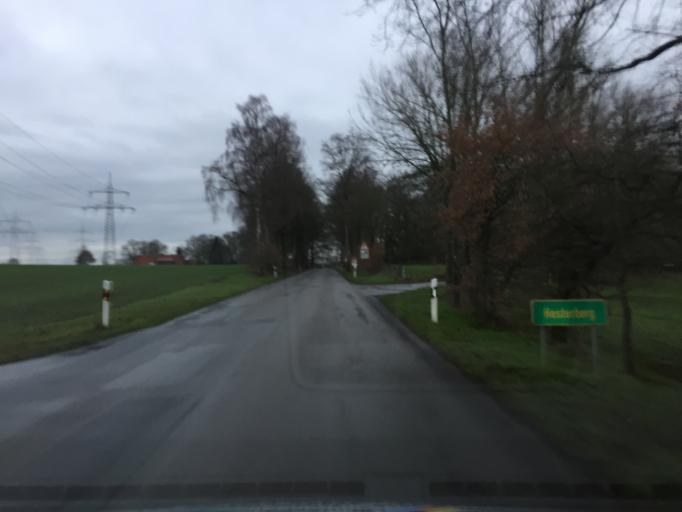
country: DE
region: Lower Saxony
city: Pennigsehl
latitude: 52.6167
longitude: 8.9926
